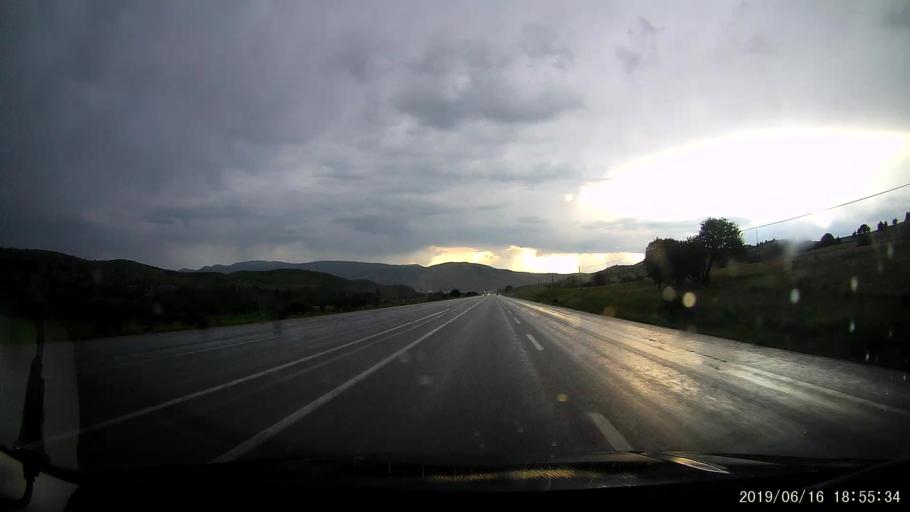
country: TR
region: Erzincan
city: Refahiye
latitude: 39.9007
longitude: 38.8244
